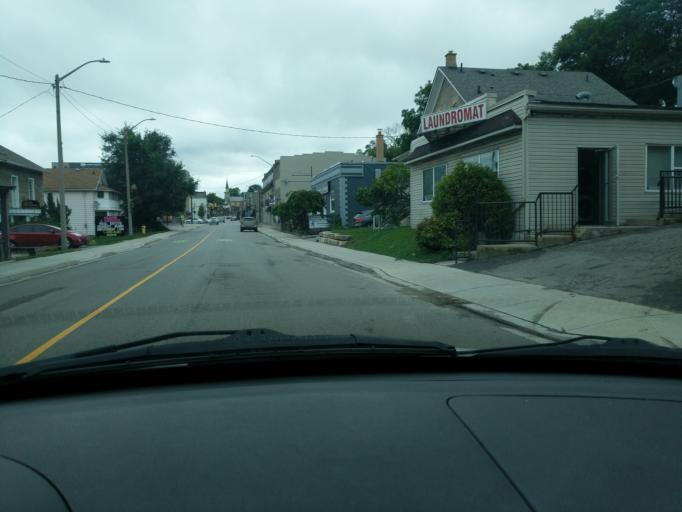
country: CA
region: Ontario
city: Cambridge
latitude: 43.4303
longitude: -80.3128
